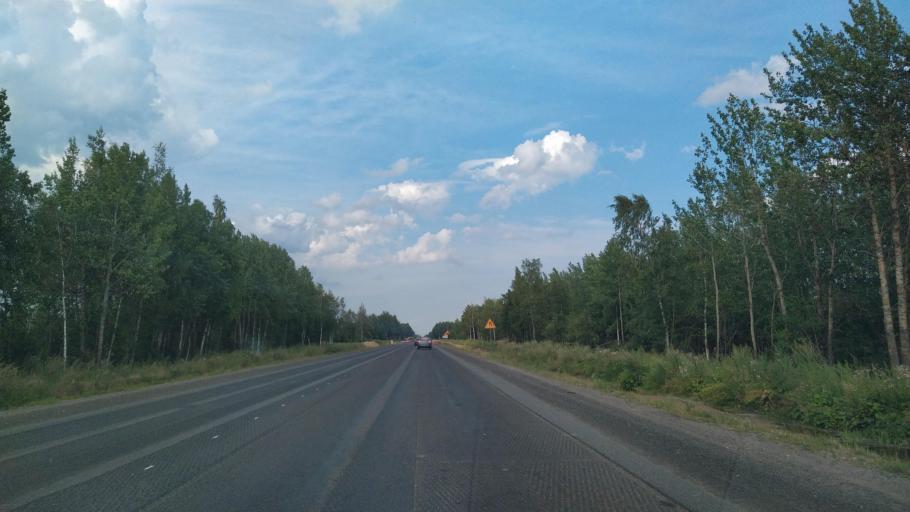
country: RU
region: Novgorod
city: Shimsk
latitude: 58.2908
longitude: 30.8593
